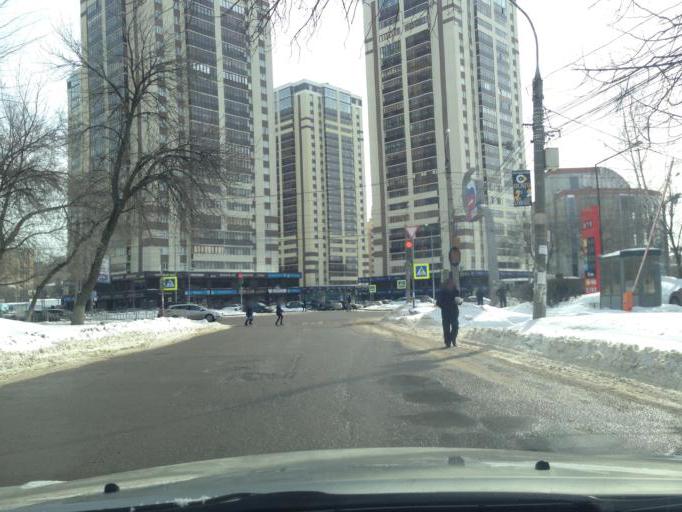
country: RU
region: Voronezj
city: Voronezh
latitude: 51.6558
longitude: 39.1779
